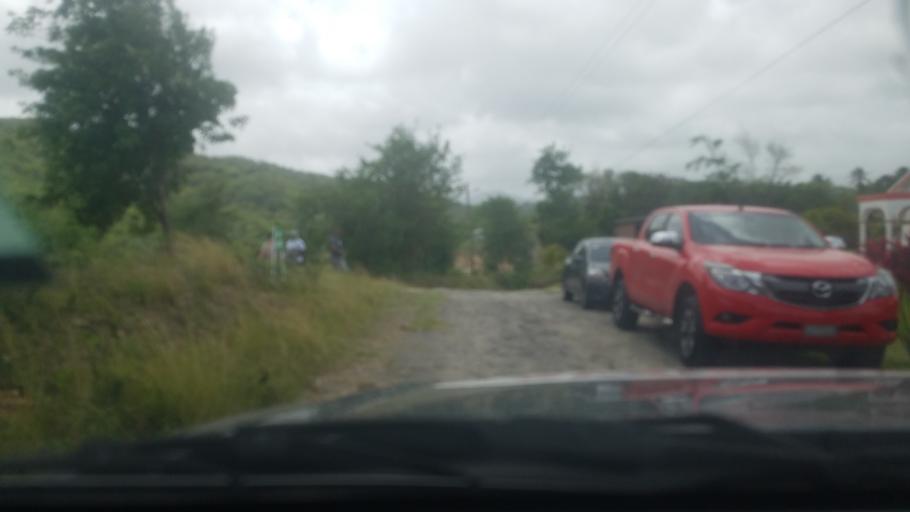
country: LC
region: Laborie Quarter
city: Laborie
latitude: 13.7565
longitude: -60.9882
